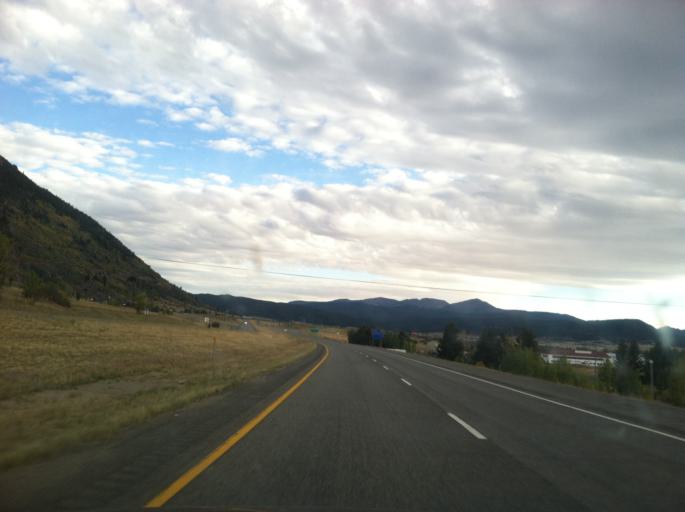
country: US
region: Montana
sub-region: Silver Bow County
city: Butte
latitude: 45.9698
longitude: -112.4755
